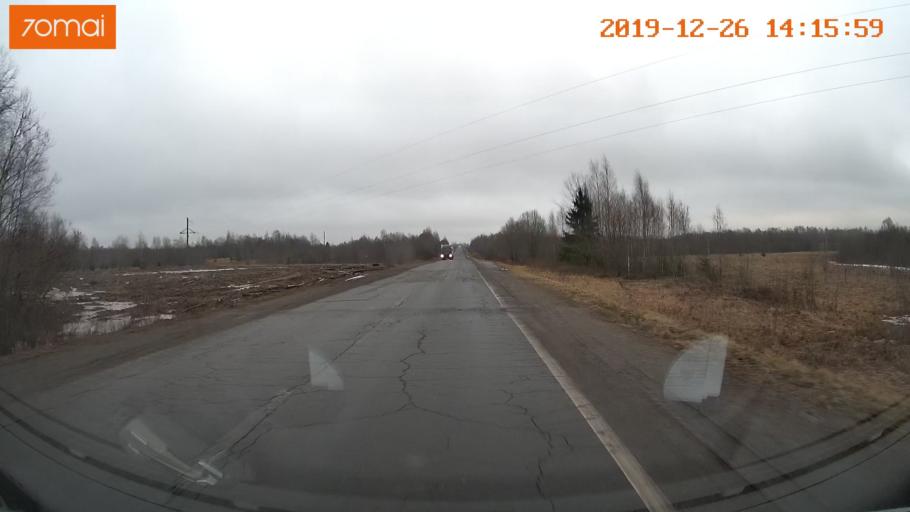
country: RU
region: Jaroslavl
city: Poshekhon'ye
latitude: 58.5163
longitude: 39.0556
